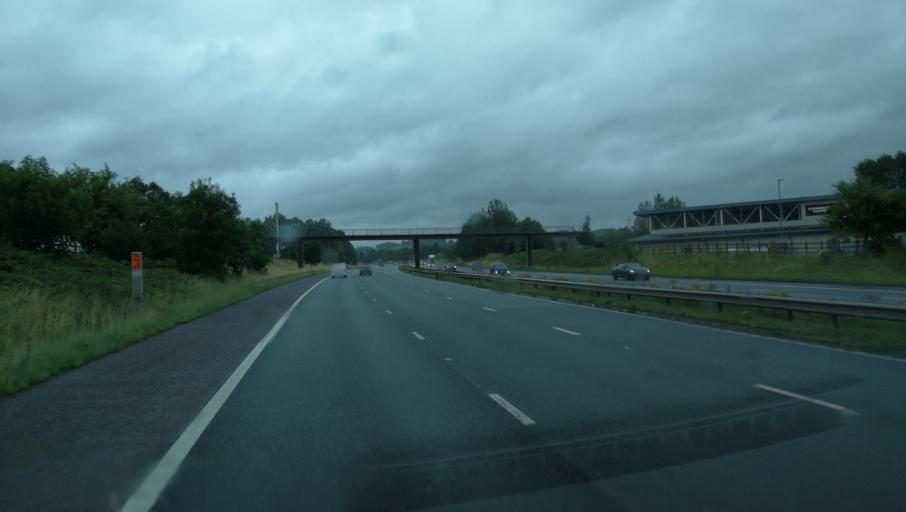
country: GB
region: England
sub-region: Borough of Bolton
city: Blackrod
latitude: 53.5993
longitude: -2.5735
